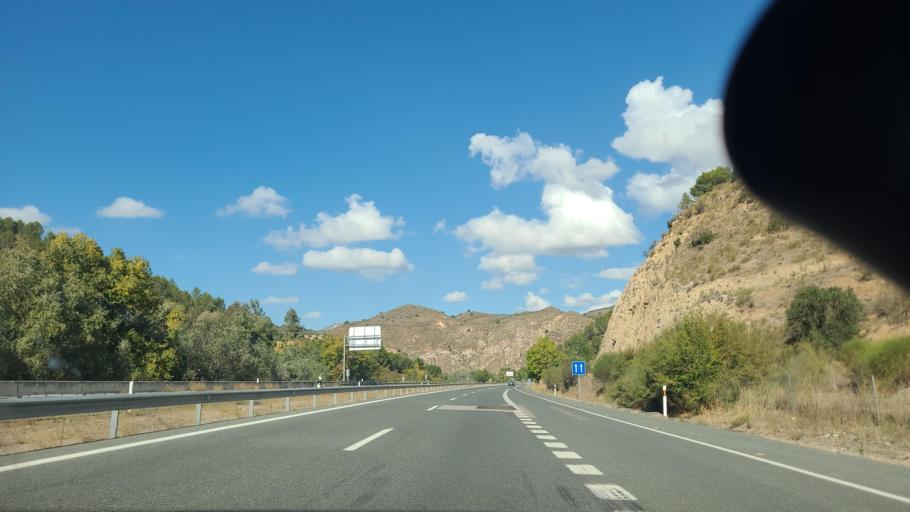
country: ES
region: Andalusia
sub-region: Provincia de Jaen
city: Cambil
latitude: 37.6475
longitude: -3.6067
